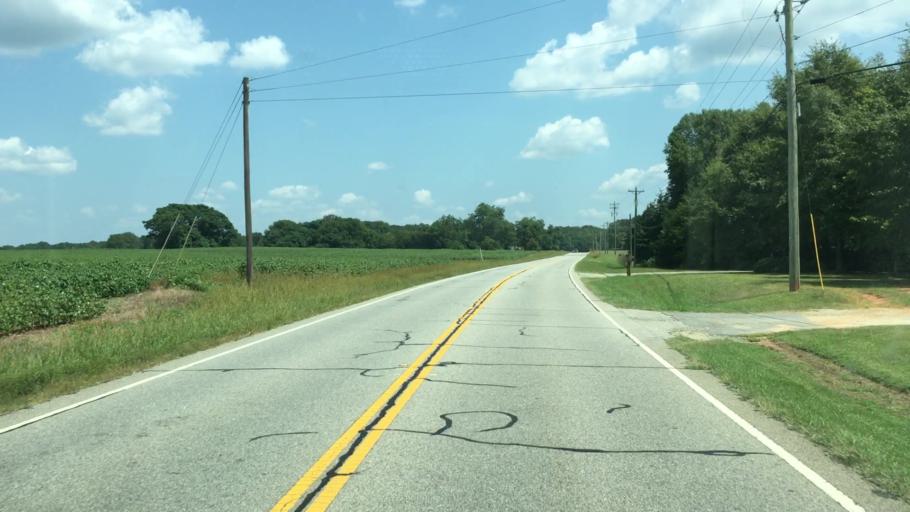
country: US
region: Georgia
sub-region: Oconee County
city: Bogart
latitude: 33.8726
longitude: -83.5116
